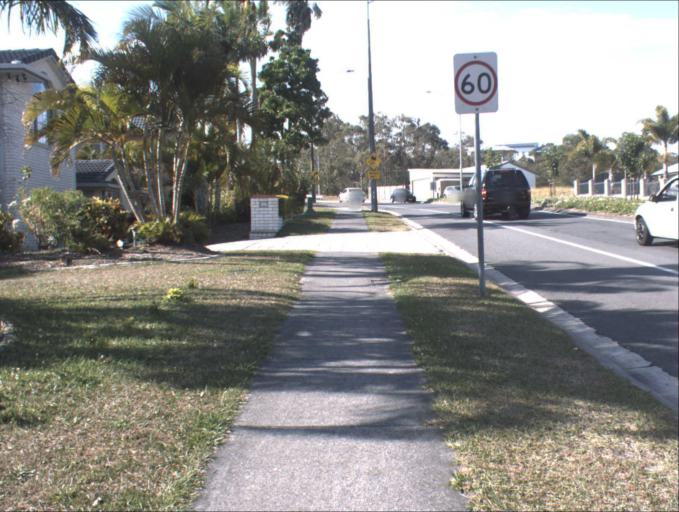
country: AU
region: Queensland
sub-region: Logan
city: Slacks Creek
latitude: -27.6504
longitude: 153.1834
